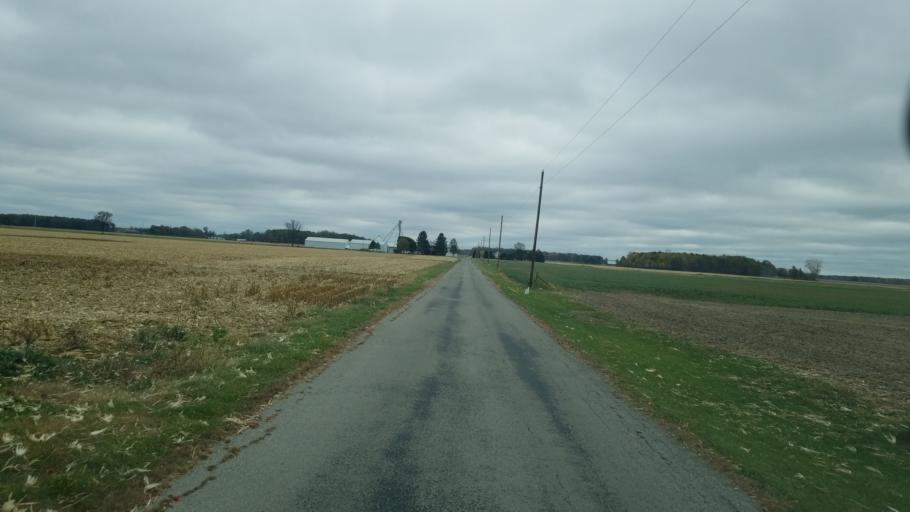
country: US
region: Ohio
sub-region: Huron County
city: Willard
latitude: 40.9314
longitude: -82.8319
